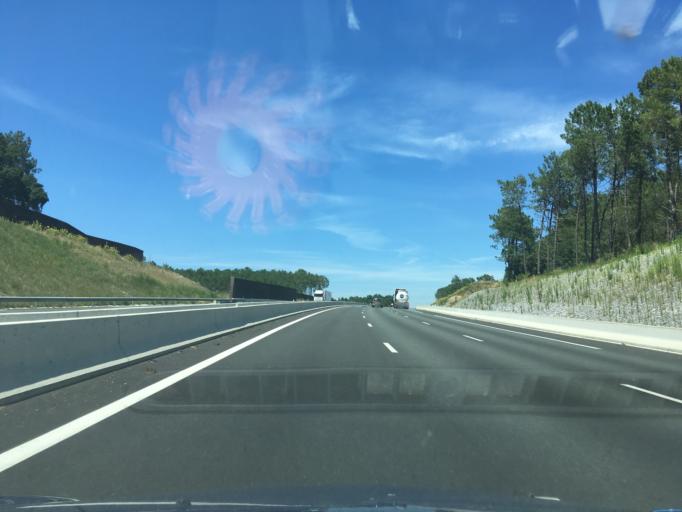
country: FR
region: Aquitaine
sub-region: Departement des Landes
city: Ondres
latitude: 43.5665
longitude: -1.4308
